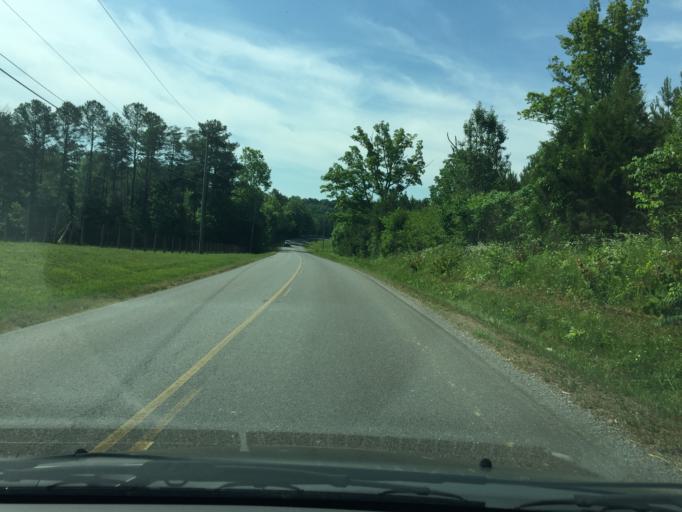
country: US
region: Tennessee
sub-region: Hamilton County
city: Collegedale
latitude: 35.1115
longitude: -85.0031
